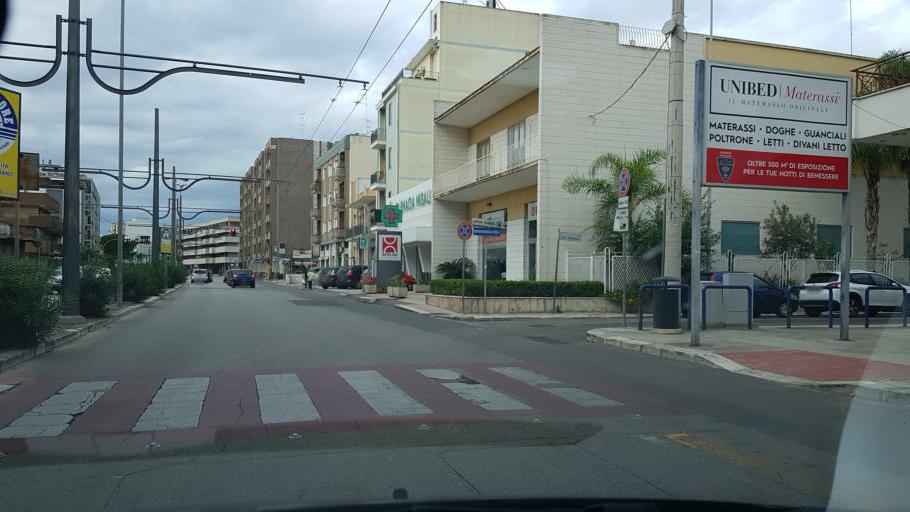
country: IT
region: Apulia
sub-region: Provincia di Lecce
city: Lecce
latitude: 40.3604
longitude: 18.1811
